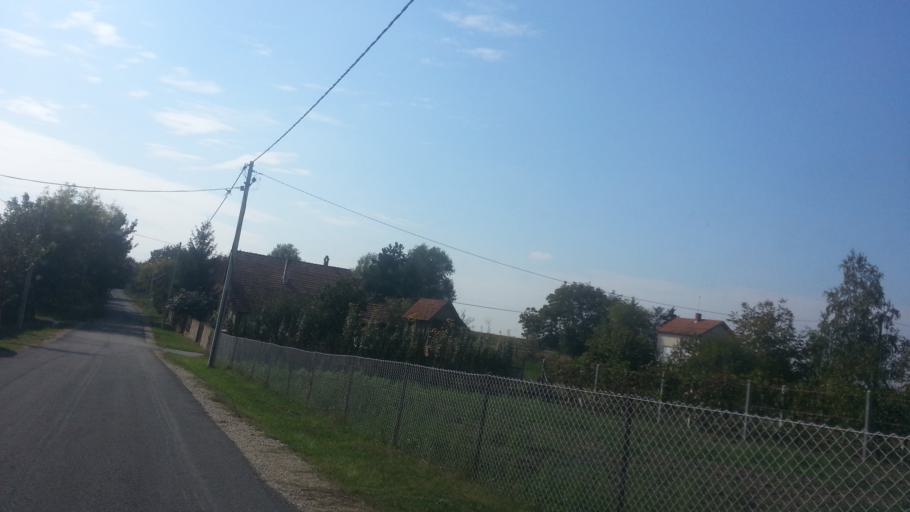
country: RS
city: Surduk
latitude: 45.0848
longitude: 20.3097
